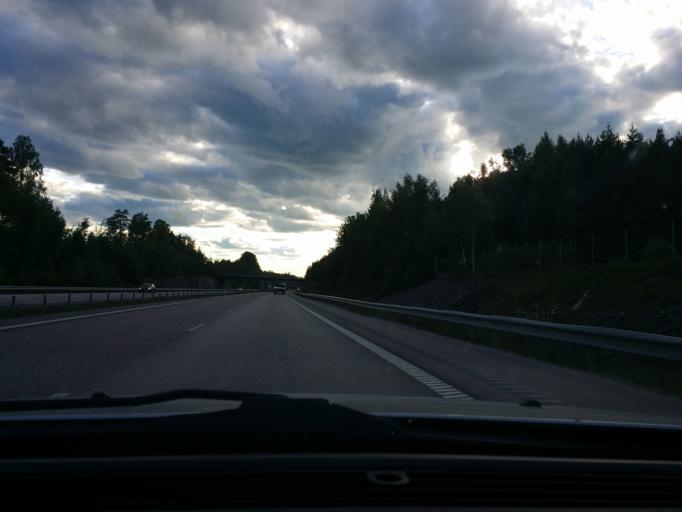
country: SE
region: Uppsala
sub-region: Enkopings Kommun
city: Enkoping
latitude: 59.6508
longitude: 17.1215
